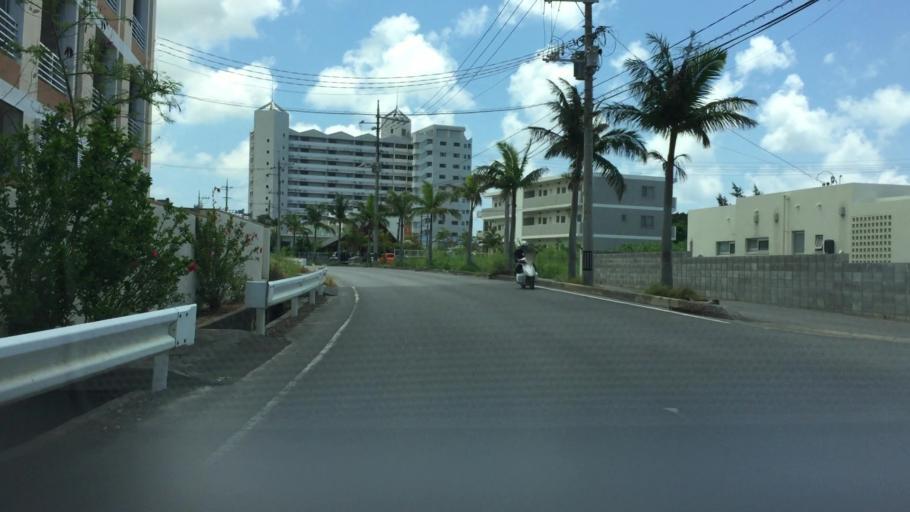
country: JP
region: Okinawa
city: Ishigaki
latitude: 24.3559
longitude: 124.1335
